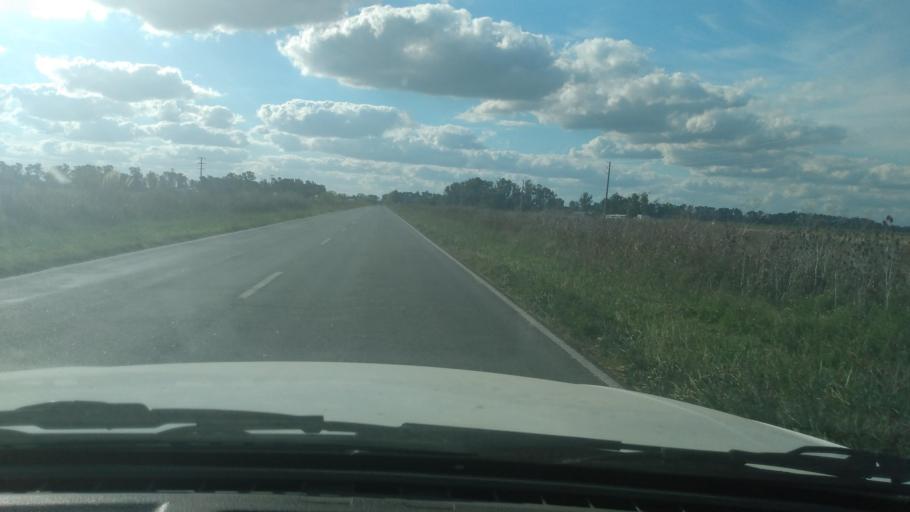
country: AR
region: Buenos Aires
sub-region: Partido de Mercedes
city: Mercedes
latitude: -34.7275
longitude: -59.3915
